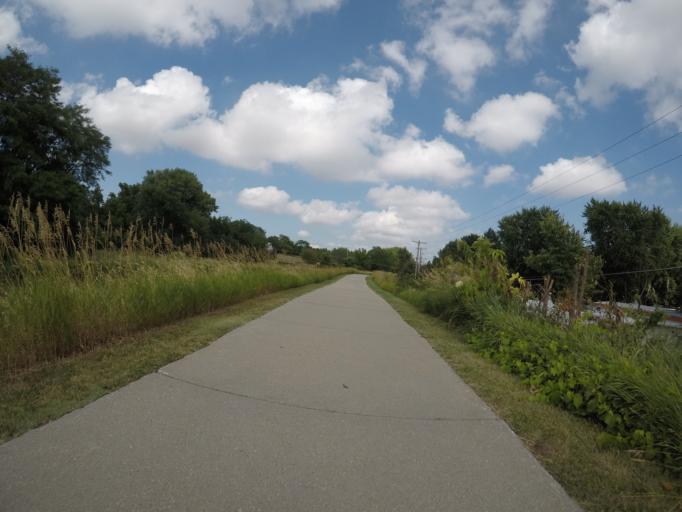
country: US
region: Nebraska
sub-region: Buffalo County
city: Kearney
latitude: 40.7014
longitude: -99.1199
